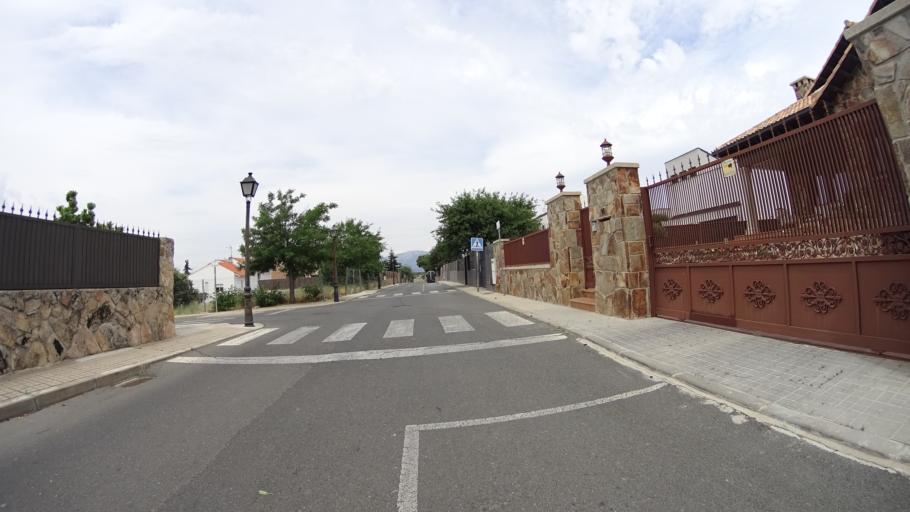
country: ES
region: Madrid
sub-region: Provincia de Madrid
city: Colmenarejo
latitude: 40.5660
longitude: -4.0154
